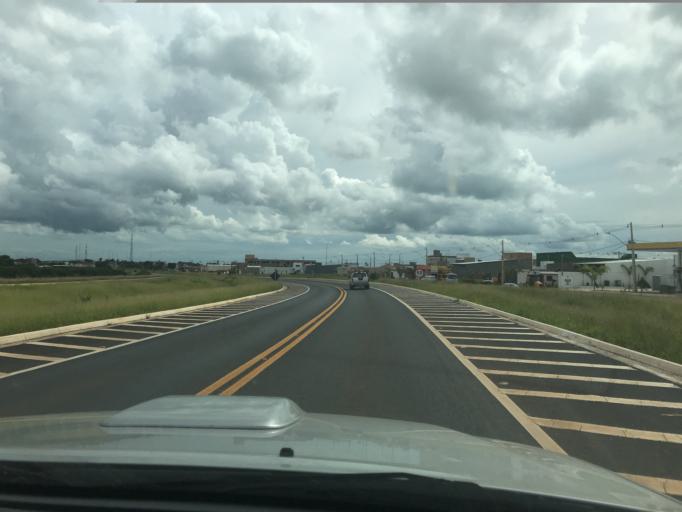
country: BR
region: Minas Gerais
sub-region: Patrocinio
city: Patrocinio
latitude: -19.0990
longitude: -46.6752
